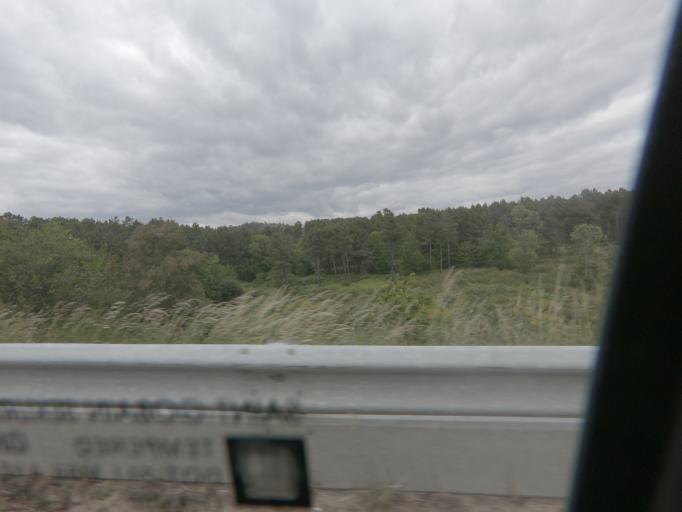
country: PT
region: Vila Real
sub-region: Sabrosa
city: Sabrosa
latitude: 41.2613
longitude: -7.6051
